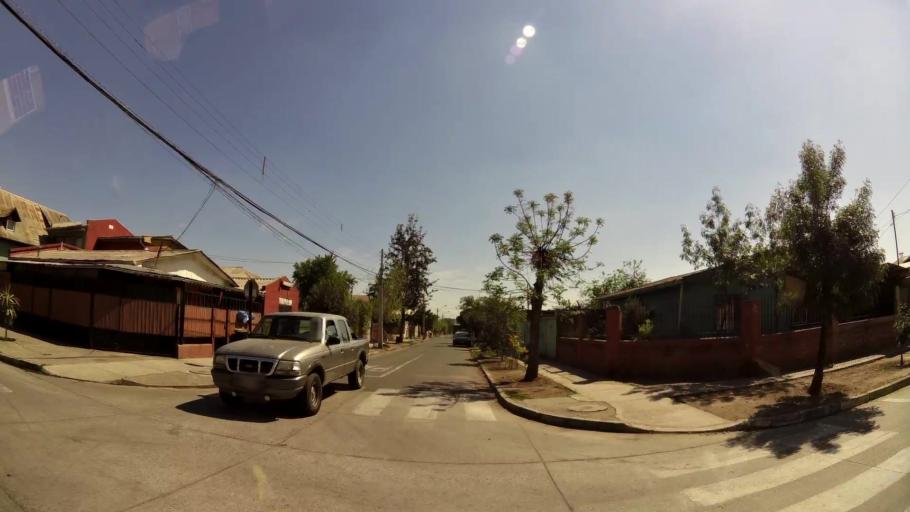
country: CL
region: Santiago Metropolitan
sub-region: Provincia de Santiago
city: La Pintana
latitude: -33.5259
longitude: -70.6383
